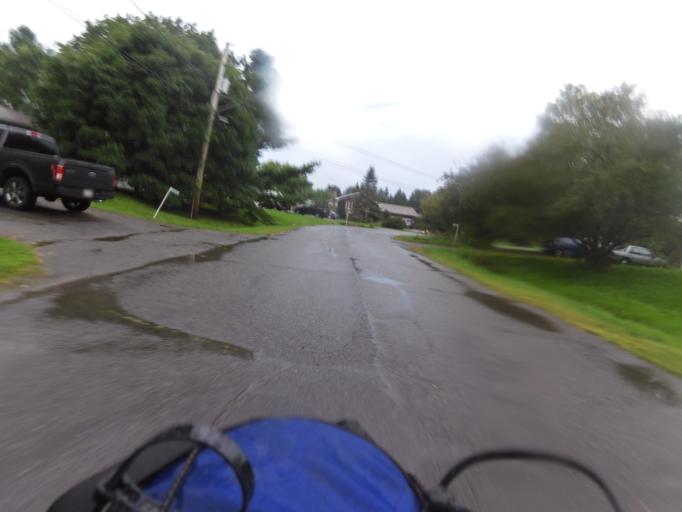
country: CA
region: Ontario
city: Ottawa
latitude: 45.2335
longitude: -75.4812
